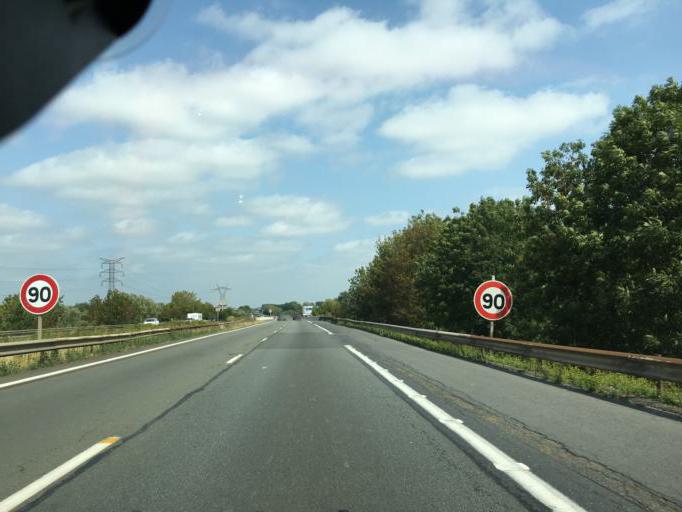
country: FR
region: Nord-Pas-de-Calais
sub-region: Departement du Nord
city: Haulchin
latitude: 50.3208
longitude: 3.4247
